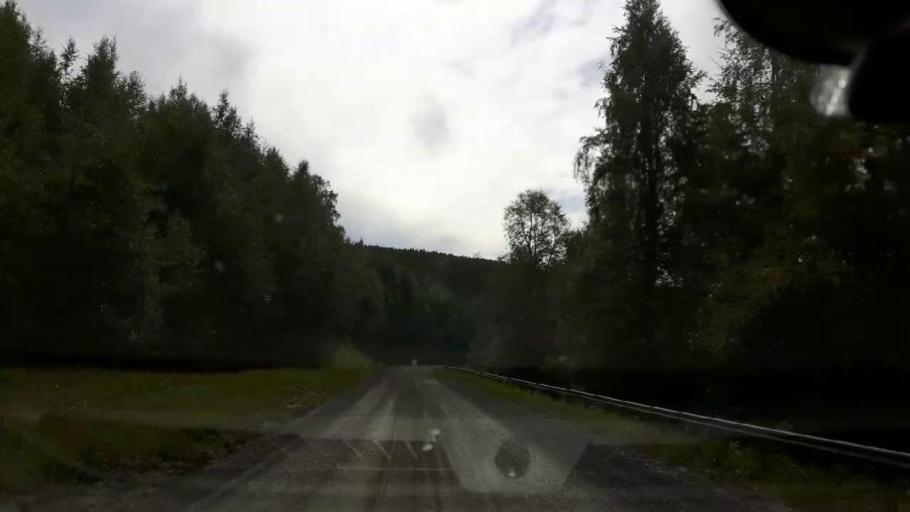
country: SE
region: Jaemtland
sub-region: Ragunda Kommun
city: Hammarstrand
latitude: 63.1333
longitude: 16.0800
